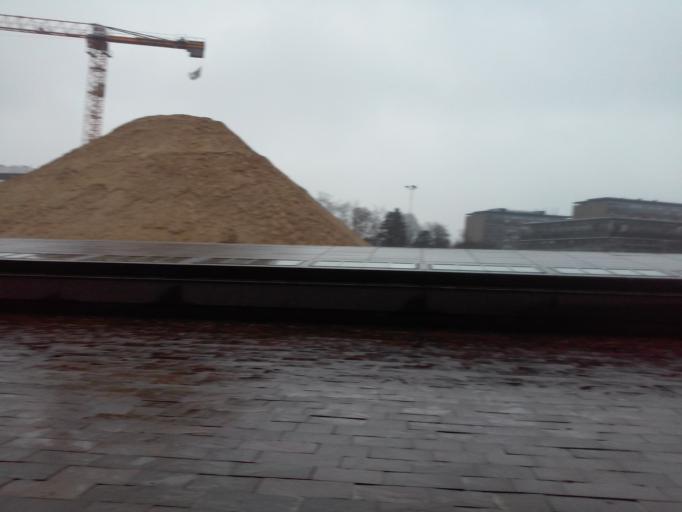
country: DK
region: Capital Region
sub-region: Kobenhavn
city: Copenhagen
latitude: 55.6993
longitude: 12.5581
